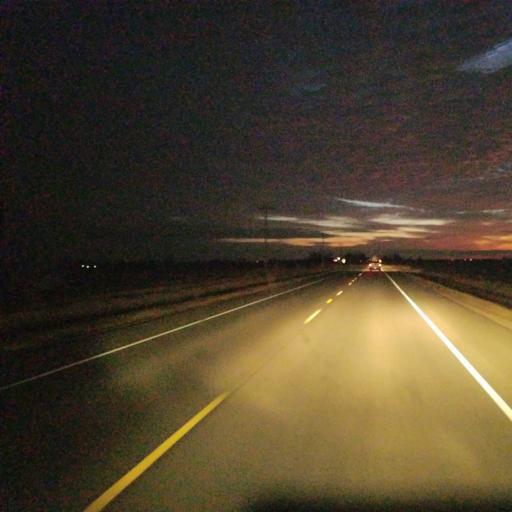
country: US
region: Illinois
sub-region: Peoria County
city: Hanna City
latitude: 40.6974
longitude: -89.8625
